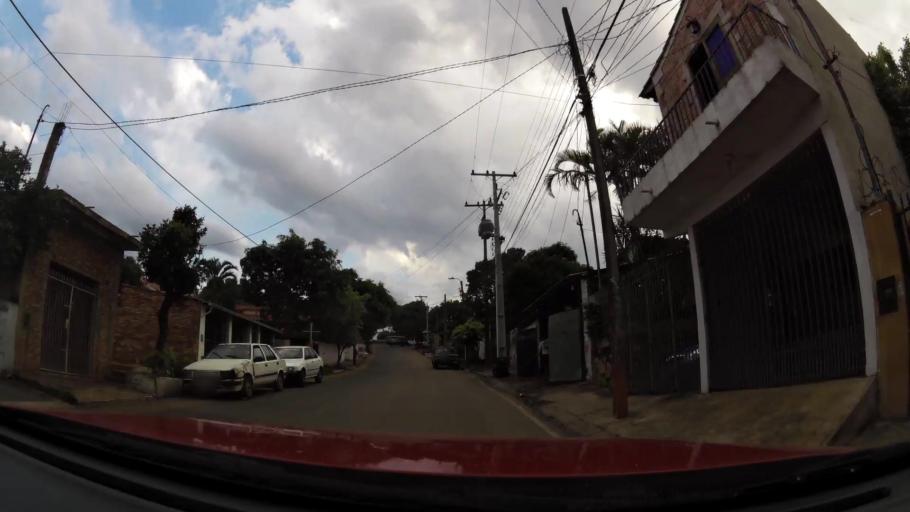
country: PY
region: Central
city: Villa Elisa
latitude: -25.3477
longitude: -57.5624
